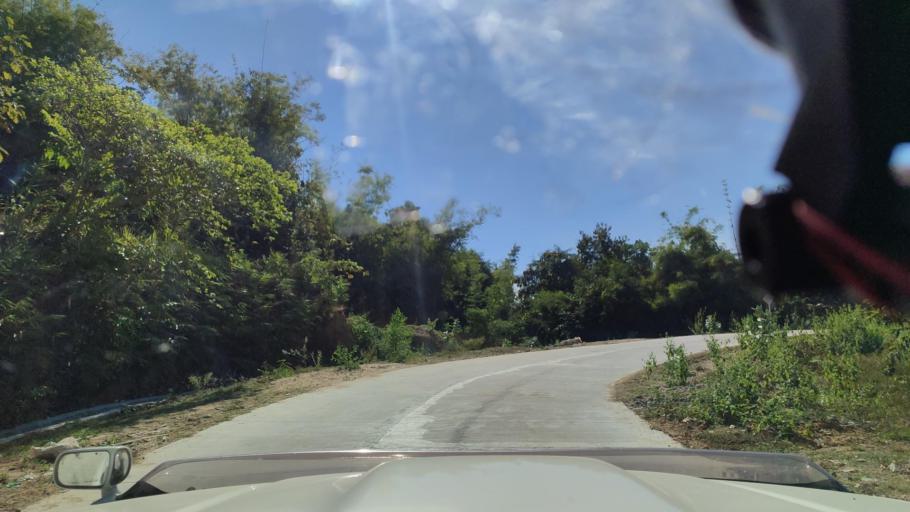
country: MM
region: Magway
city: Taungdwingyi
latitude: 19.9320
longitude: 95.8222
